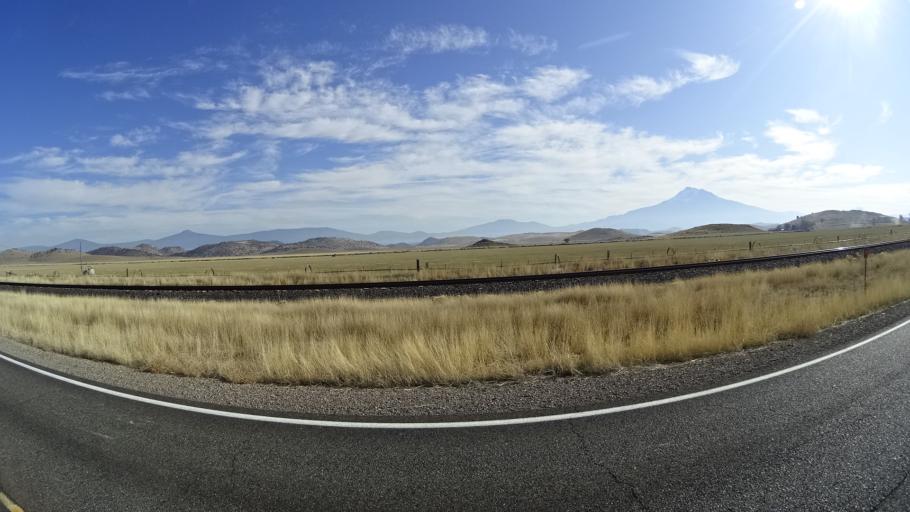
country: US
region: California
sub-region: Siskiyou County
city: Montague
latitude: 41.5702
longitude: -122.5252
